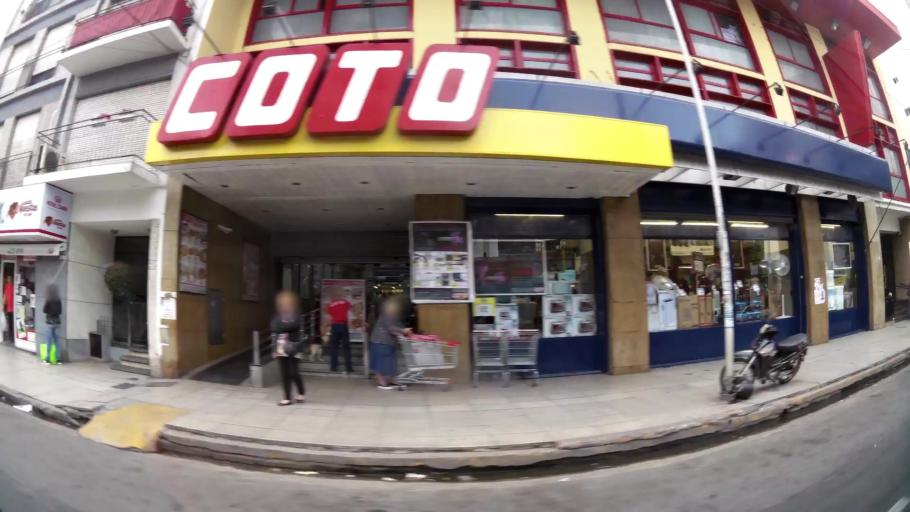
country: AR
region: Buenos Aires
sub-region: Partido de Avellaneda
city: Avellaneda
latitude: -34.6651
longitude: -58.3625
